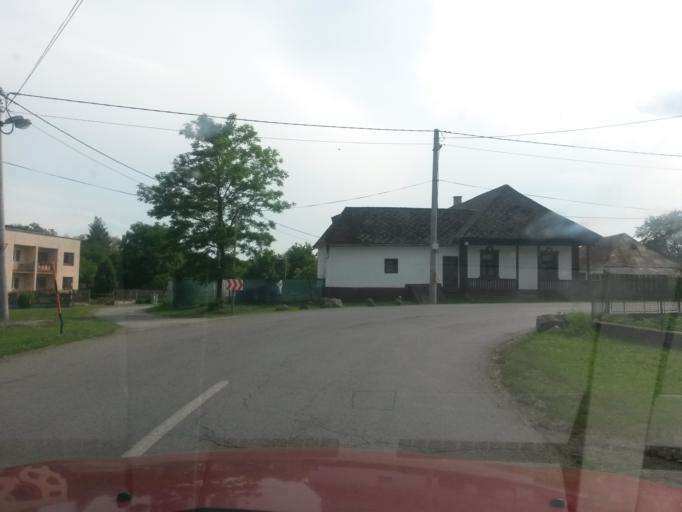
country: SK
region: Presovsky
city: Snina
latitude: 49.0137
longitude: 22.0362
